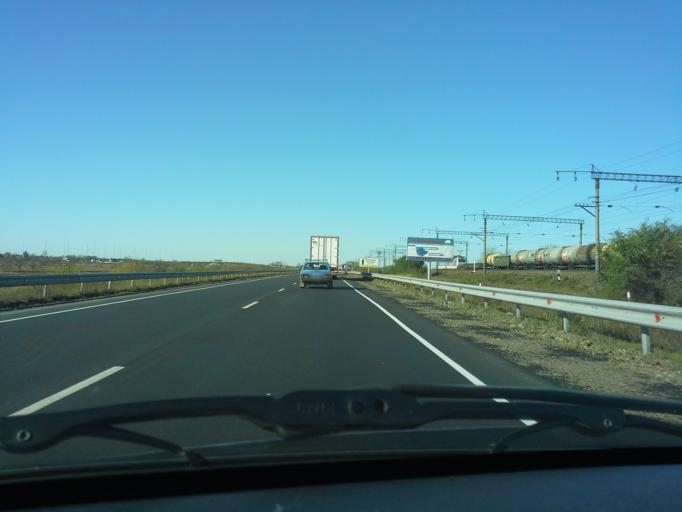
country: RU
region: Jewish Autonomous Oblast
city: Priamurskiy
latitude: 48.5264
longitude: 134.9373
